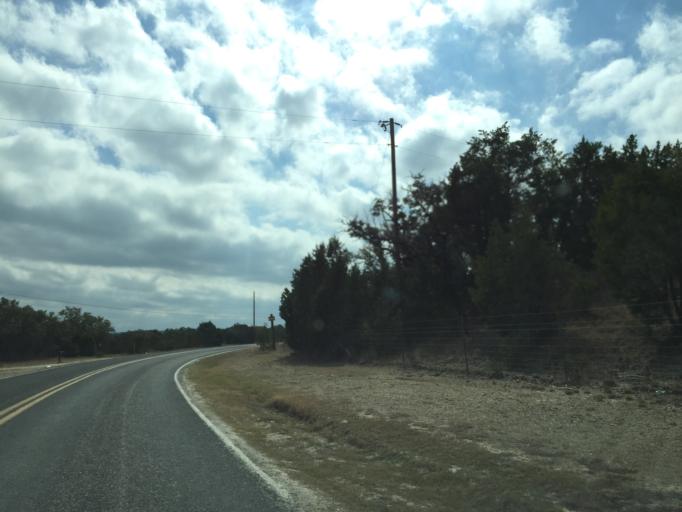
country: US
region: Texas
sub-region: Travis County
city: Briarcliff
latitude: 30.3809
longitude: -98.0945
